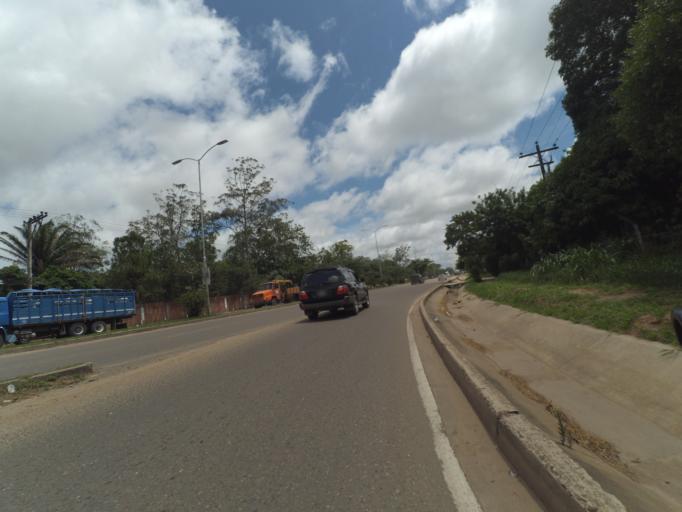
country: BO
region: Santa Cruz
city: Santa Rita
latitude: -17.8699
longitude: -63.2737
